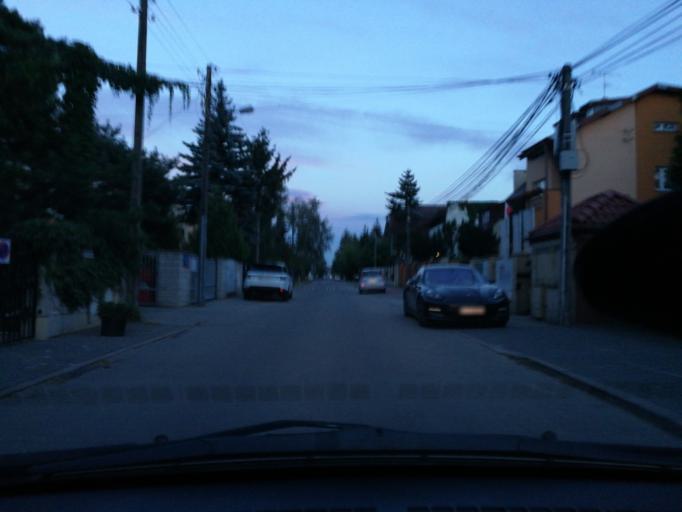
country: PL
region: Masovian Voivodeship
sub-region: Warszawa
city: Wilanow
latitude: 52.1754
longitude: 21.0725
